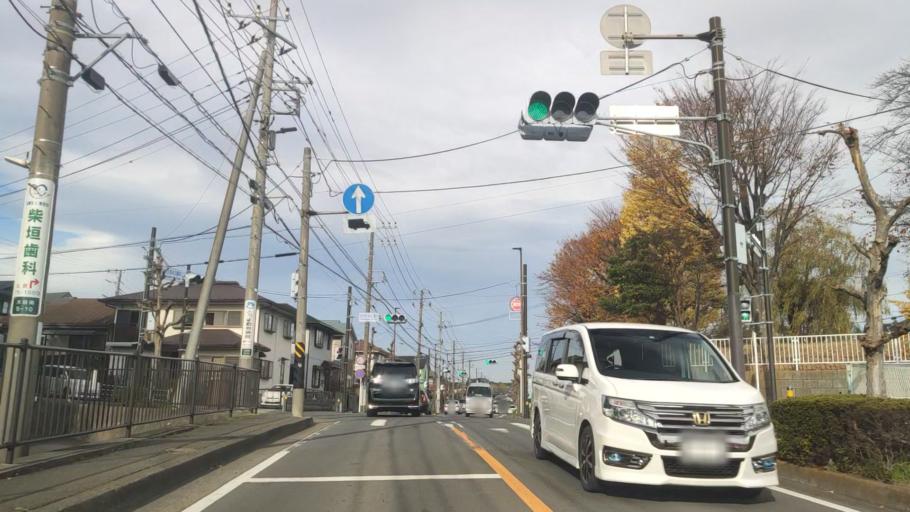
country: JP
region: Kanagawa
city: Atsugi
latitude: 35.4332
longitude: 139.4047
